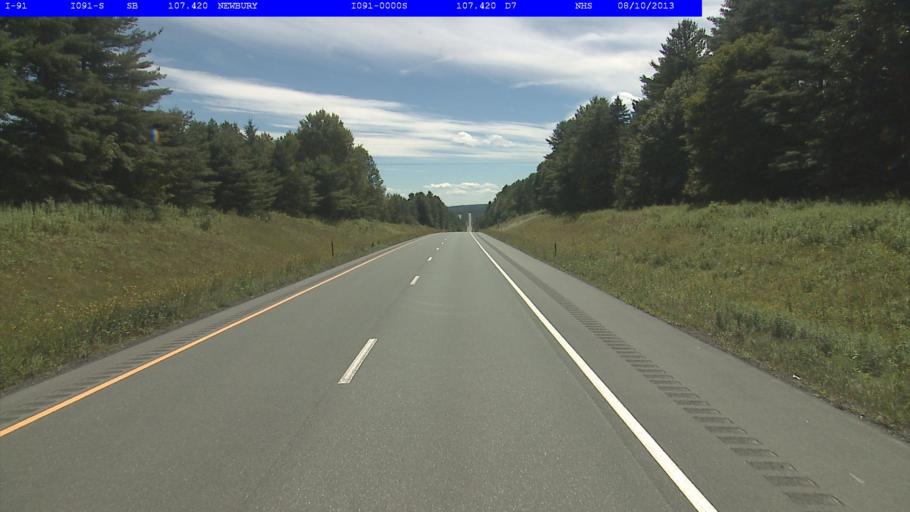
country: US
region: New Hampshire
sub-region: Grafton County
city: Woodsville
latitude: 44.1206
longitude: -72.1056
